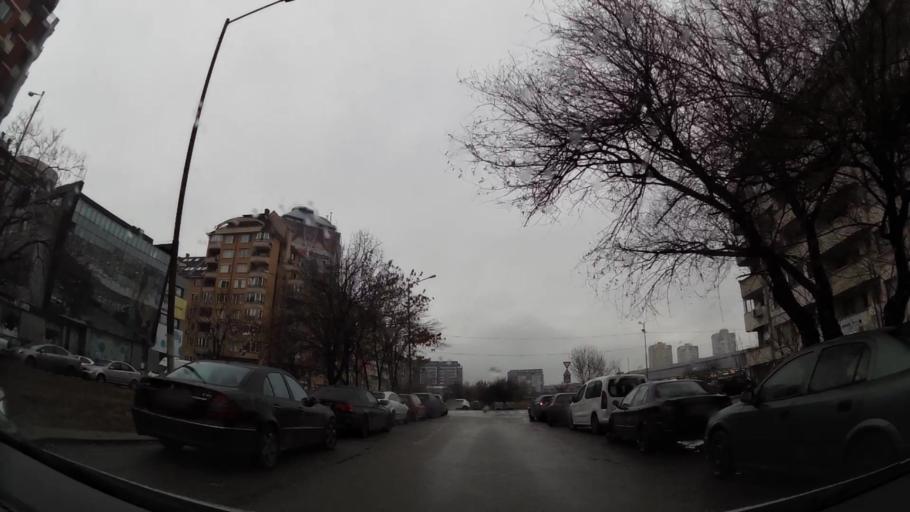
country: BG
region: Sofia-Capital
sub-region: Stolichna Obshtina
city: Sofia
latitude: 42.6354
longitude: 23.3757
